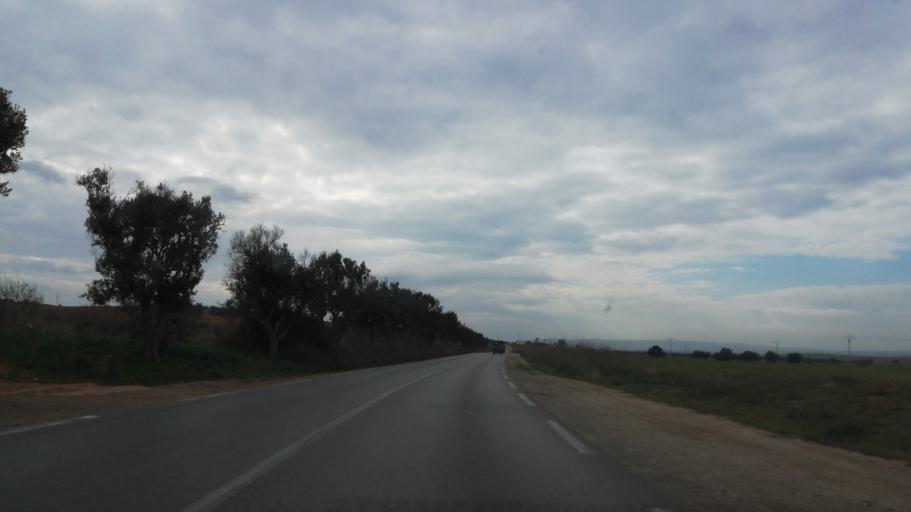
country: DZ
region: Oran
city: Ain el Bya
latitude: 35.7538
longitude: -0.3512
